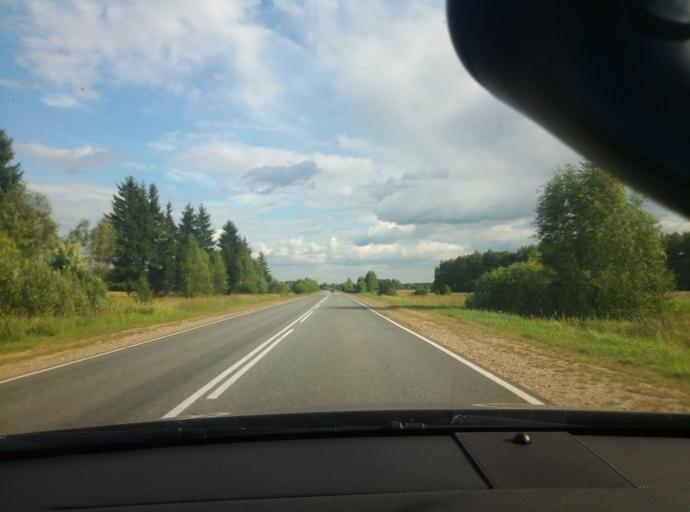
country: RU
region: Kaluga
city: Yukhnov
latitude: 54.6119
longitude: 35.3565
